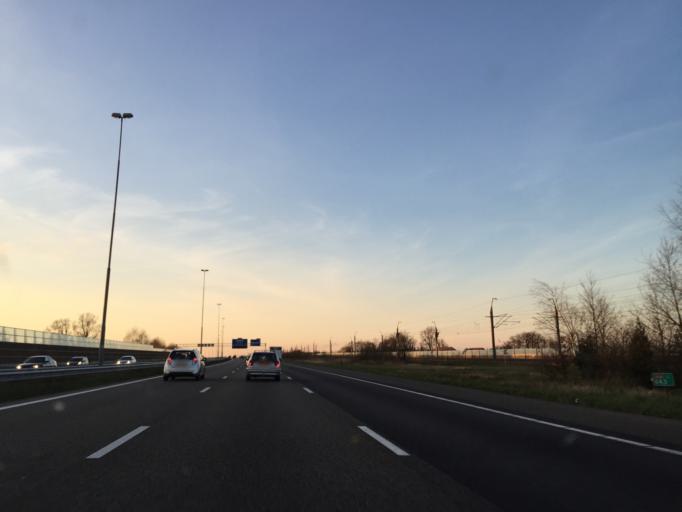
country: NL
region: North Brabant
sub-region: Gemeente Breda
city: Breda
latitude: 51.5538
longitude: 4.7384
